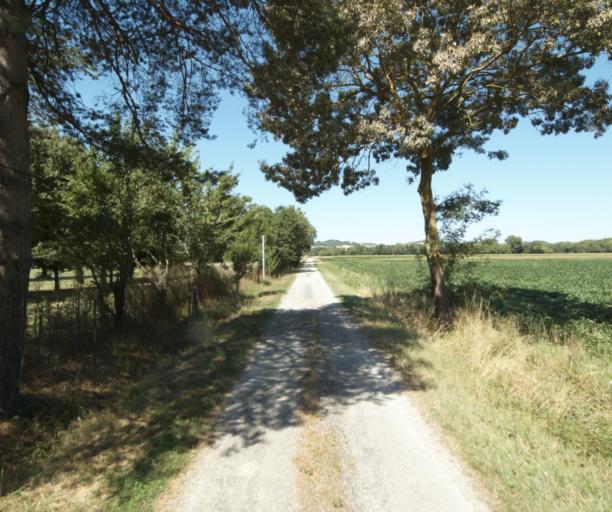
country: FR
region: Midi-Pyrenees
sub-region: Departement de la Haute-Garonne
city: Revel
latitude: 43.4909
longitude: 1.9677
